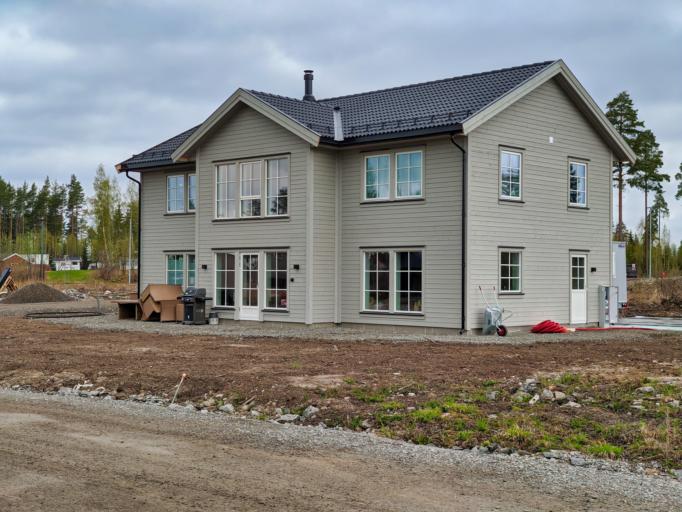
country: NO
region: Hedmark
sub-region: Loten
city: Loten
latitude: 60.7898
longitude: 11.3232
